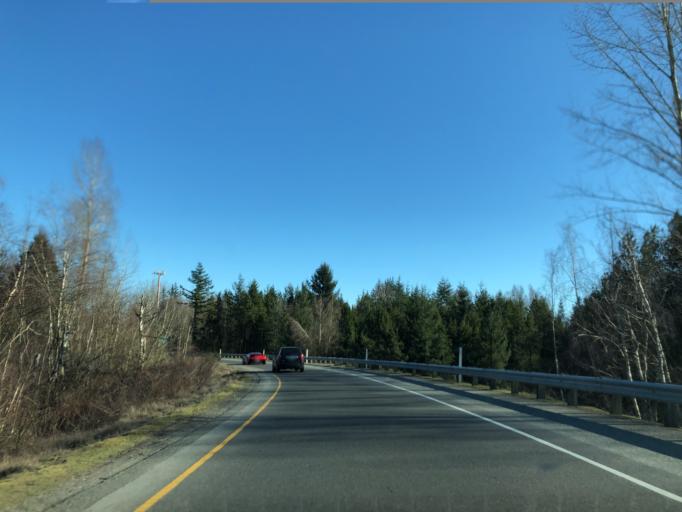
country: US
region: Washington
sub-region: Whatcom County
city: Birch Bay
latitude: 48.9342
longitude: -122.6635
